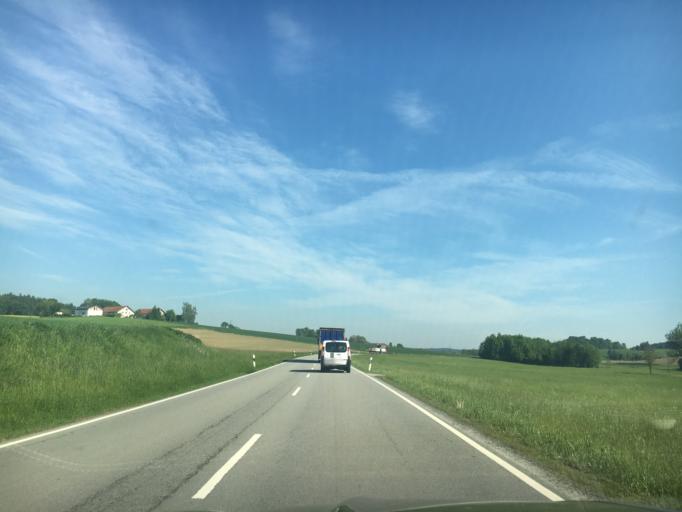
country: DE
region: Bavaria
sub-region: Upper Bavaria
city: Rohrbach
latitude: 48.3031
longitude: 12.5629
